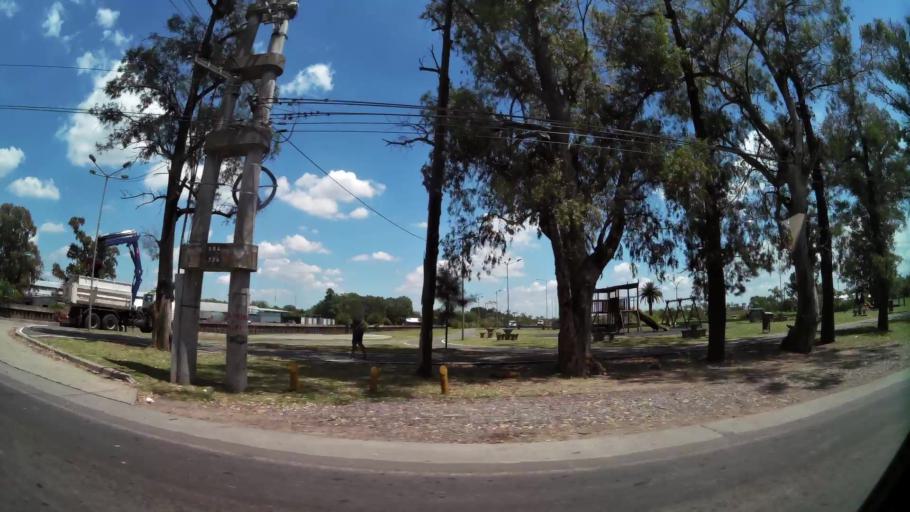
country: AR
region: Buenos Aires
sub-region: Partido de Tigre
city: Tigre
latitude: -34.4409
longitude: -58.5966
